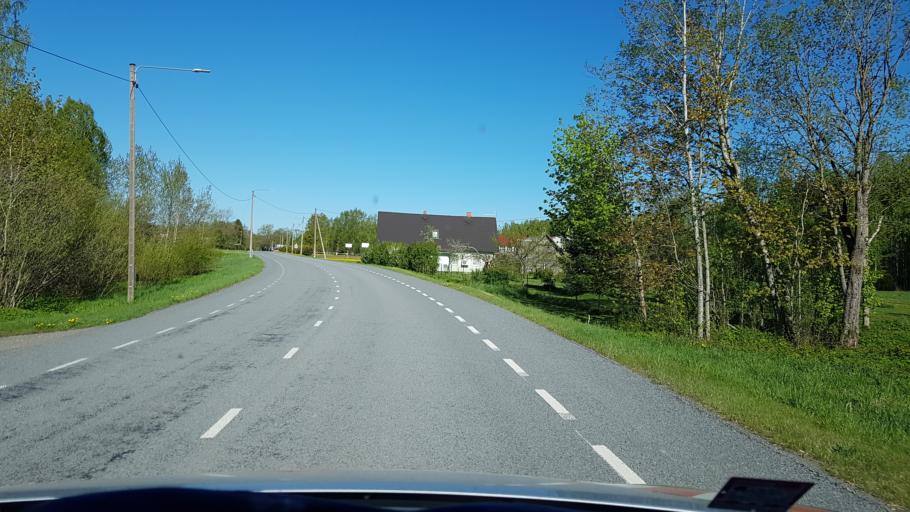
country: EE
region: Polvamaa
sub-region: Polva linn
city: Polva
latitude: 58.2816
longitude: 27.0557
